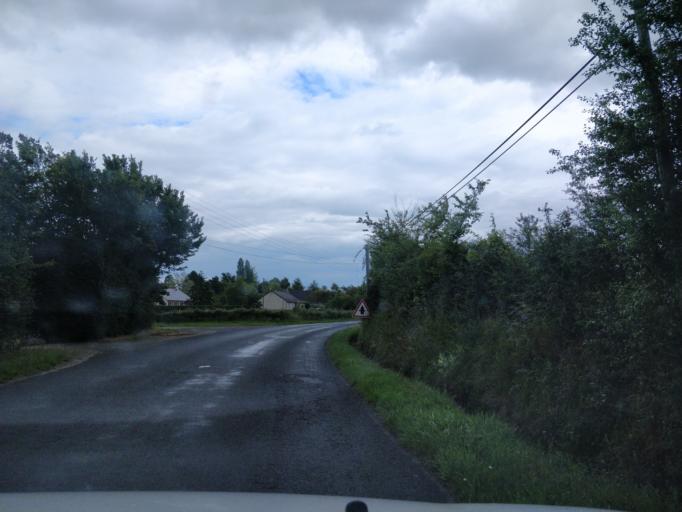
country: FR
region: Pays de la Loire
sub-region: Departement de Maine-et-Loire
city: Grez-Neuville
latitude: 47.6393
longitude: -0.6518
